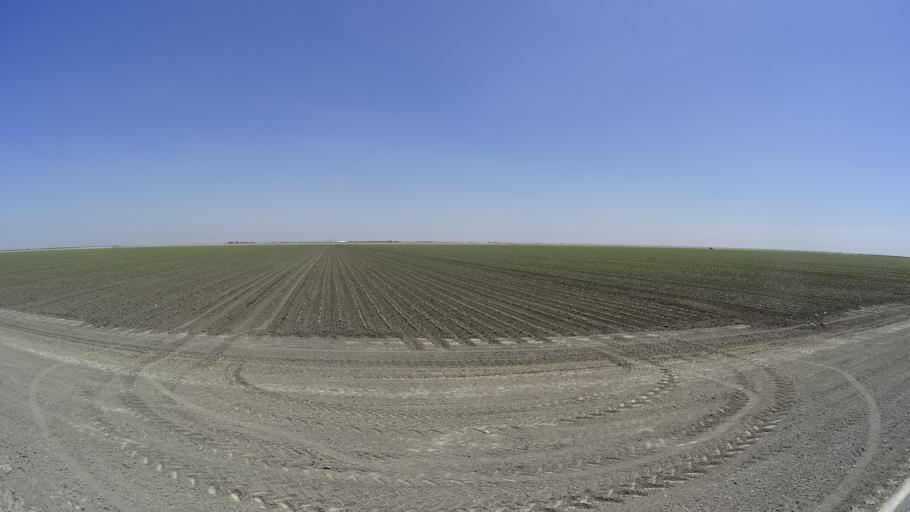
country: US
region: California
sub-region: Kings County
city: Corcoran
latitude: 36.0910
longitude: -119.6441
